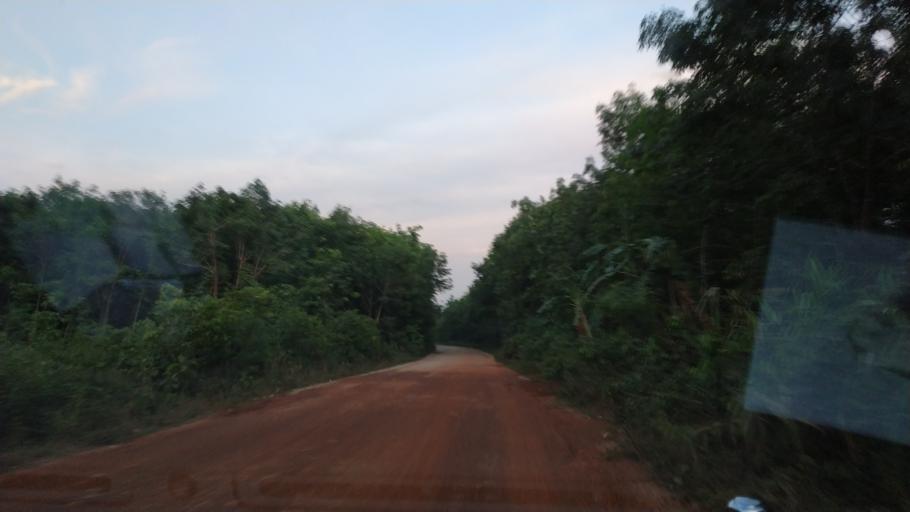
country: MM
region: Mon
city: Kyaikto
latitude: 17.4195
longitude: 97.0523
